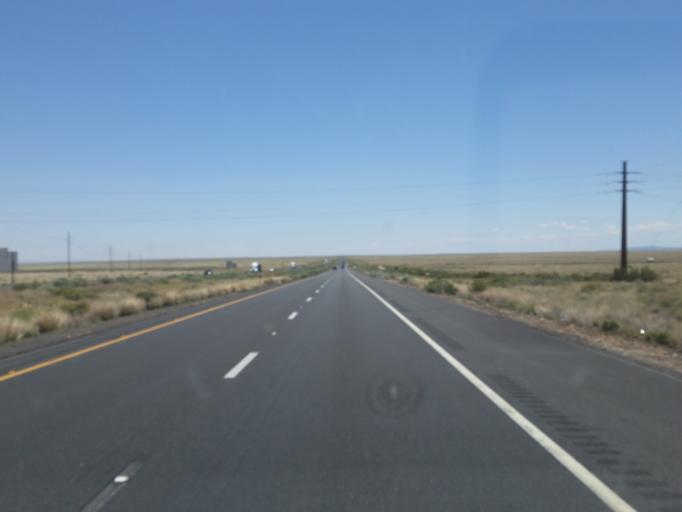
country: US
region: Arizona
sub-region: Coconino County
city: Flagstaff
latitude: 35.1554
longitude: -111.2560
